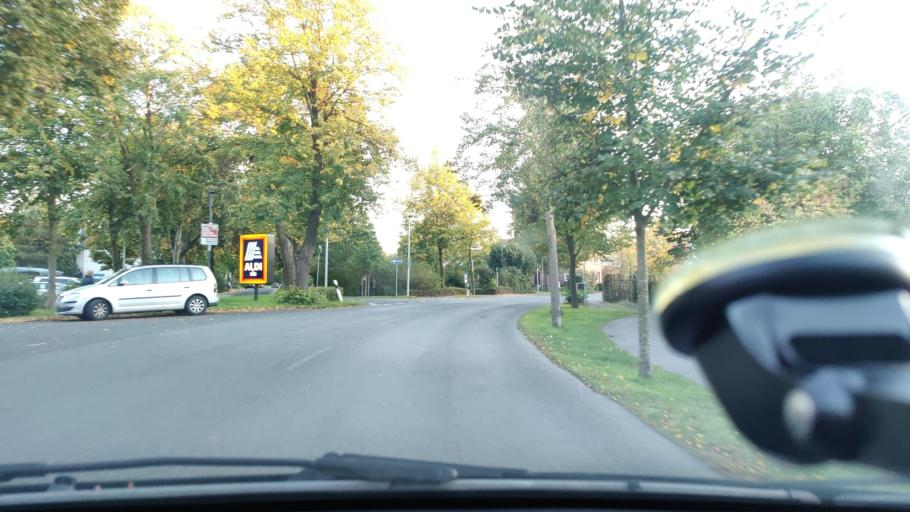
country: DE
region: North Rhine-Westphalia
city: Kalkar
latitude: 51.7341
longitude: 6.2962
